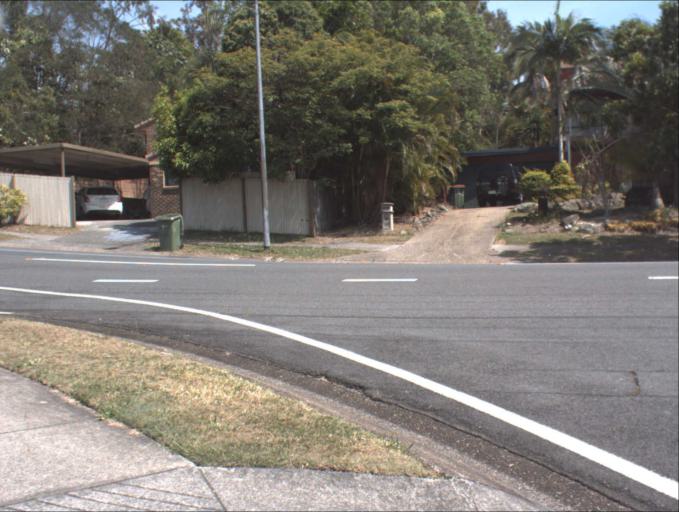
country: AU
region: Queensland
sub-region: Logan
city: Slacks Creek
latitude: -27.6582
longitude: 153.1871
